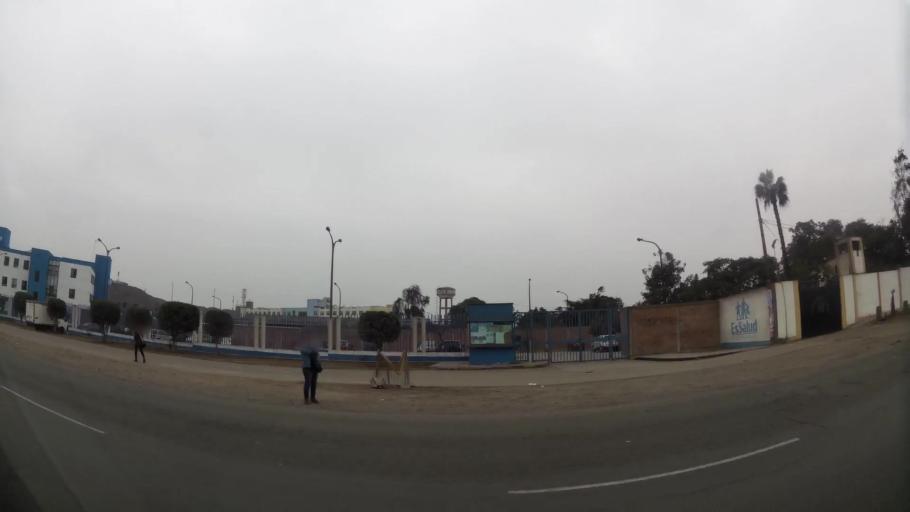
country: PE
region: Lima
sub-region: Lima
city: Vitarte
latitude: -12.0472
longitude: -76.9466
